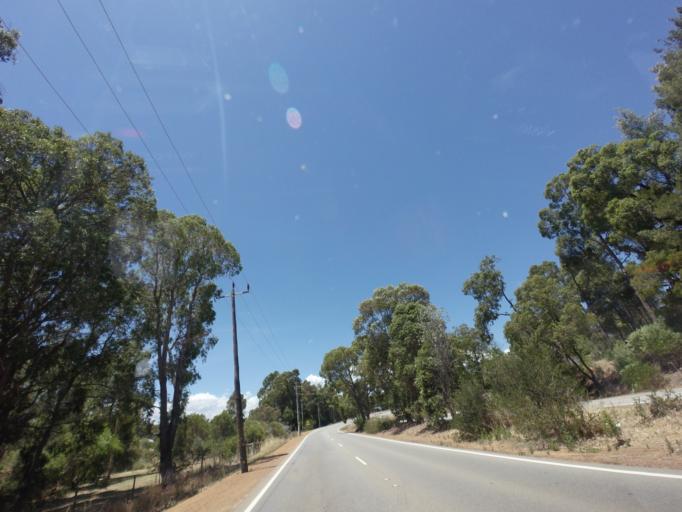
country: AU
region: Western Australia
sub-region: Mundaring
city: Parkerville
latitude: -31.8994
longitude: 116.1381
